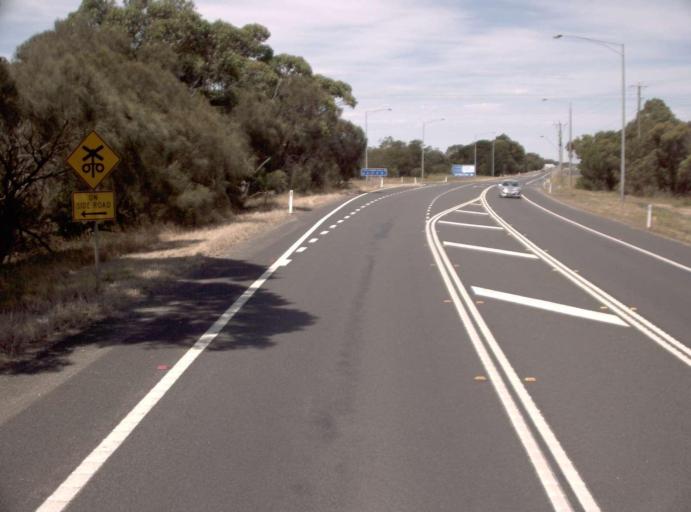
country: AU
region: Victoria
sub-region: Wellington
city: Sale
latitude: -38.0989
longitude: 146.9756
